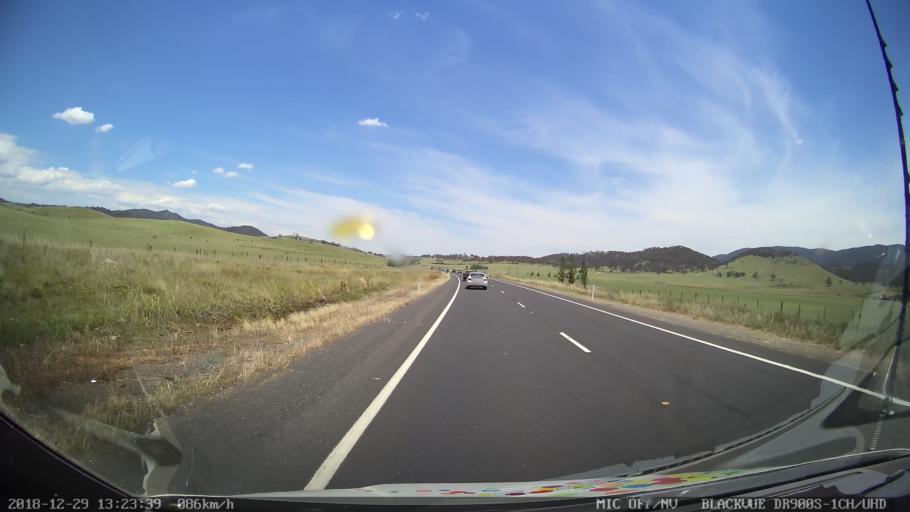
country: AU
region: Australian Capital Territory
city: Macarthur
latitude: -35.8195
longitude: 149.1636
